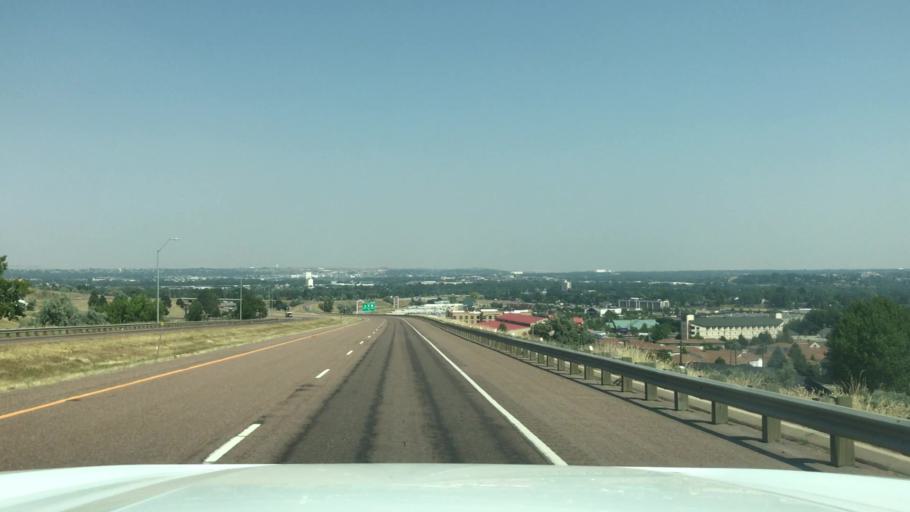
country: US
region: Montana
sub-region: Cascade County
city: Great Falls
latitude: 47.4783
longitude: -111.3518
